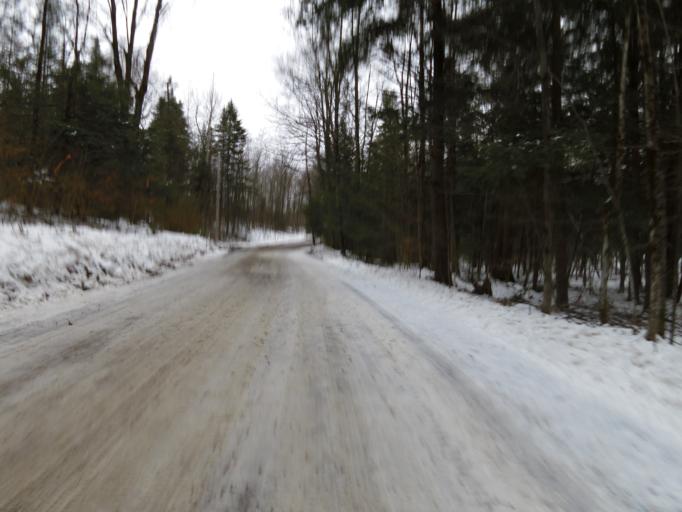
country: CA
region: Ontario
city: Carleton Place
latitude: 45.1822
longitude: -76.2246
